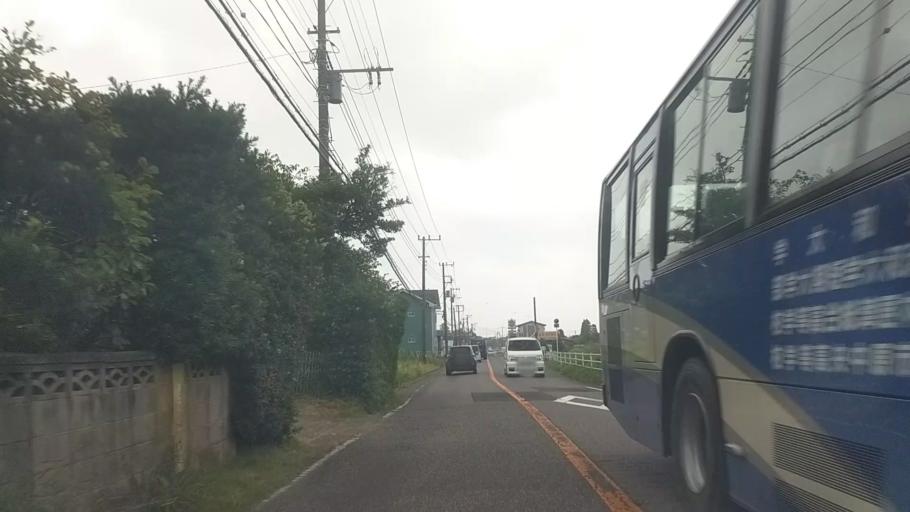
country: JP
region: Chiba
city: Ohara
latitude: 35.2606
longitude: 140.3783
